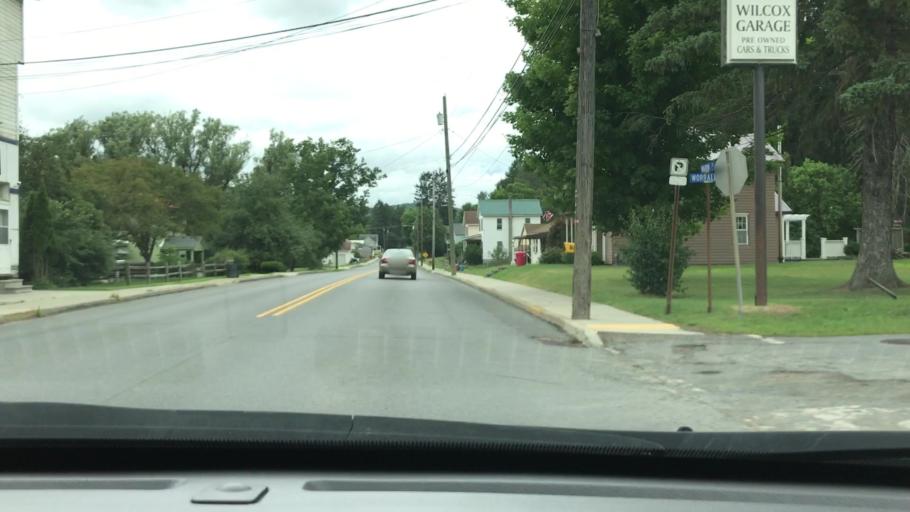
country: US
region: Pennsylvania
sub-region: Elk County
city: Johnsonburg
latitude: 41.5762
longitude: -78.6884
